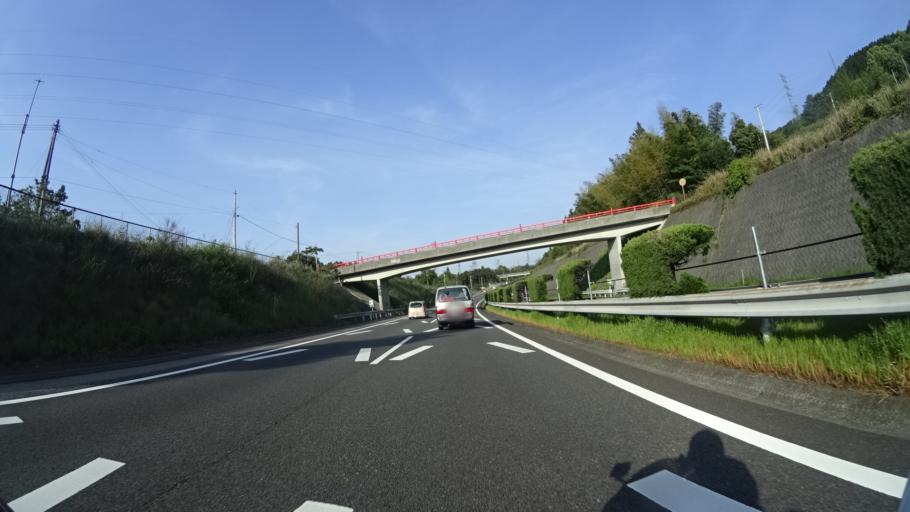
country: JP
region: Ehime
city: Niihama
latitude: 33.9396
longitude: 133.3838
